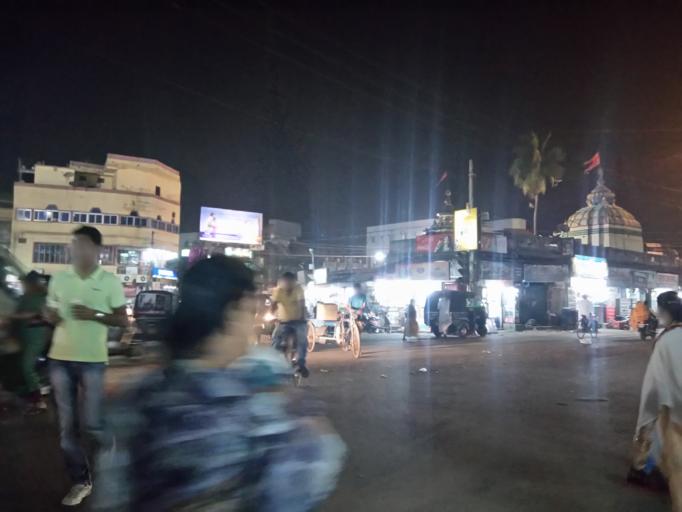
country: IN
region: Odisha
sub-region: Cuttack
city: Cuttack
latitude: 20.4607
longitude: 85.8828
